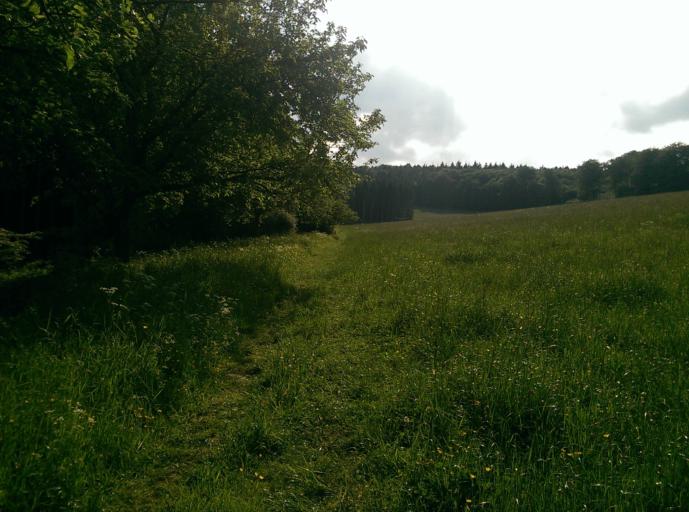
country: DE
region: Rheinland-Pfalz
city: Melsbach
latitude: 50.4889
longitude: 7.4580
